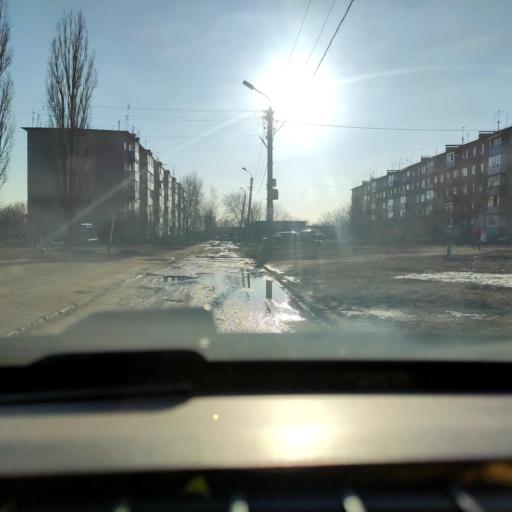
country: RU
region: Voronezj
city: Maslovka
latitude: 51.5356
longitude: 39.3412
